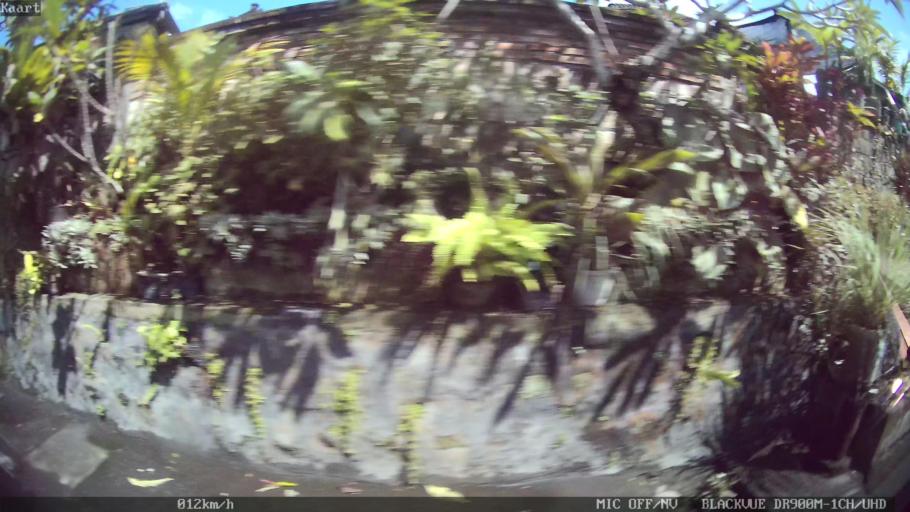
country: ID
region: Bali
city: Banjar Tebongkang
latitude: -8.5437
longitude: 115.2693
